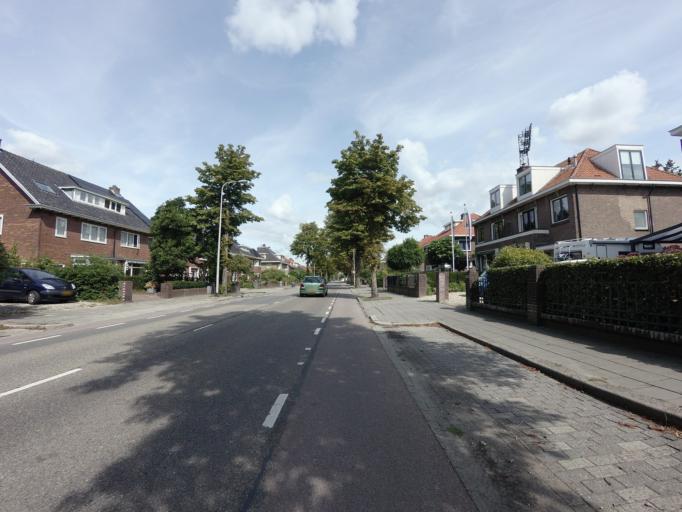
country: NL
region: Overijssel
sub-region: Gemeente Deventer
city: Deventer
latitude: 52.2610
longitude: 6.1710
